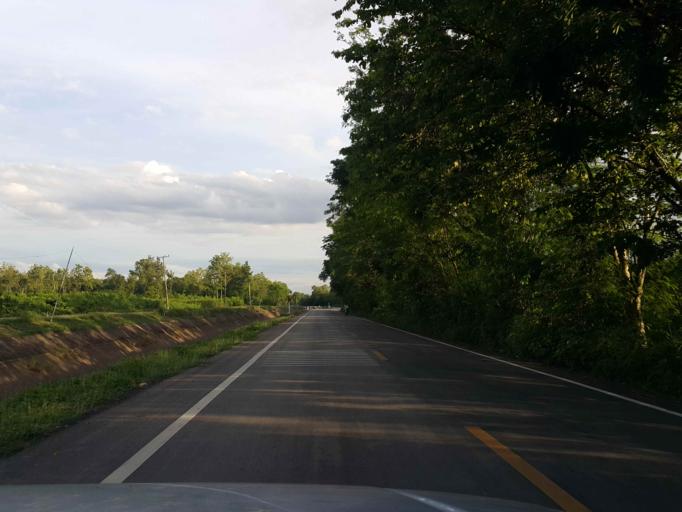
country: TH
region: Chiang Mai
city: San Sai
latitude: 18.9266
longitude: 99.1432
